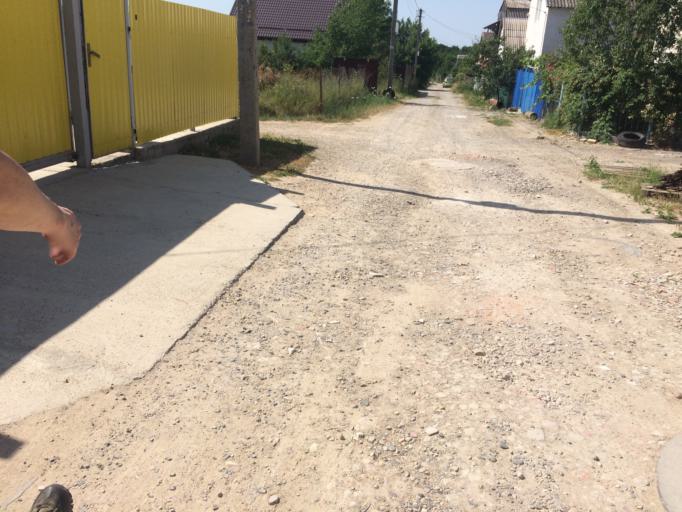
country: RU
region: Stavropol'skiy
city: Tatarka
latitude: 44.9821
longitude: 41.9411
